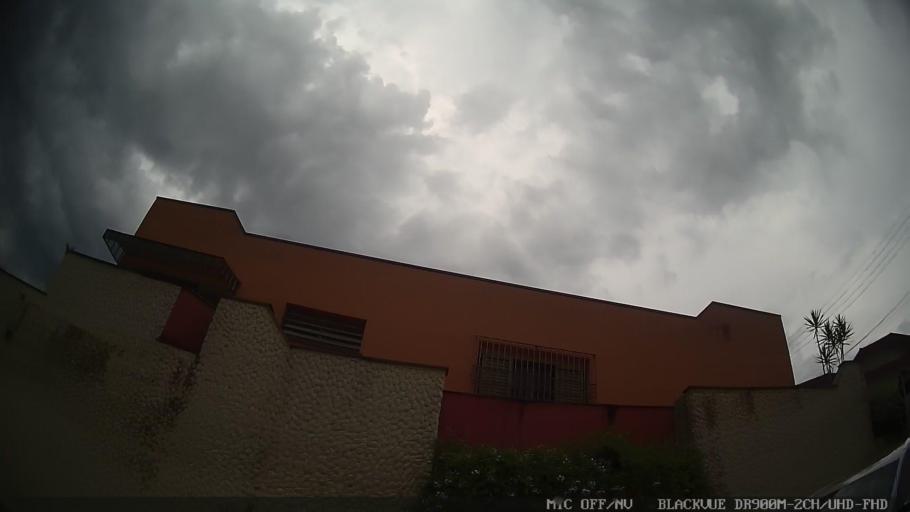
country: BR
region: Sao Paulo
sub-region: Itatiba
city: Itatiba
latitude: -23.0089
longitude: -46.8367
